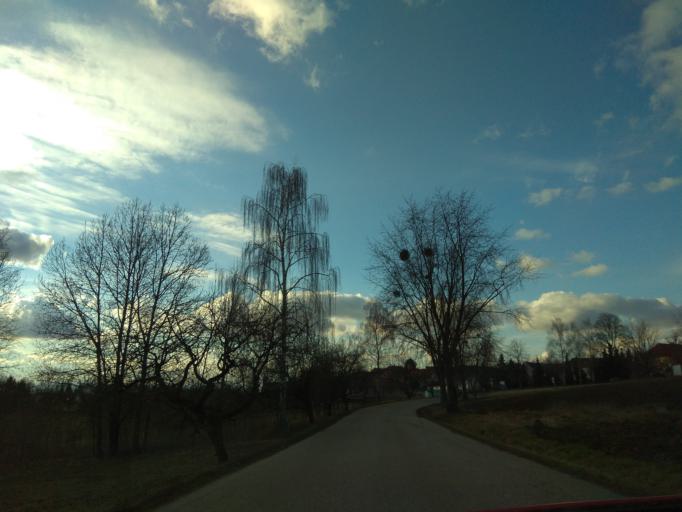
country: CZ
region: Jihocesky
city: Hrdejovice
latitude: 49.0345
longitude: 14.4787
